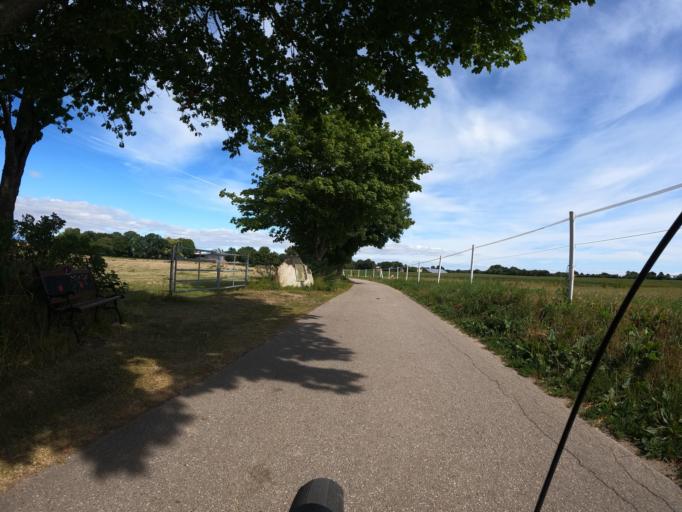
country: DE
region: Schleswig-Holstein
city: Steinbergkirche
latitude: 54.7668
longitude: 9.7597
